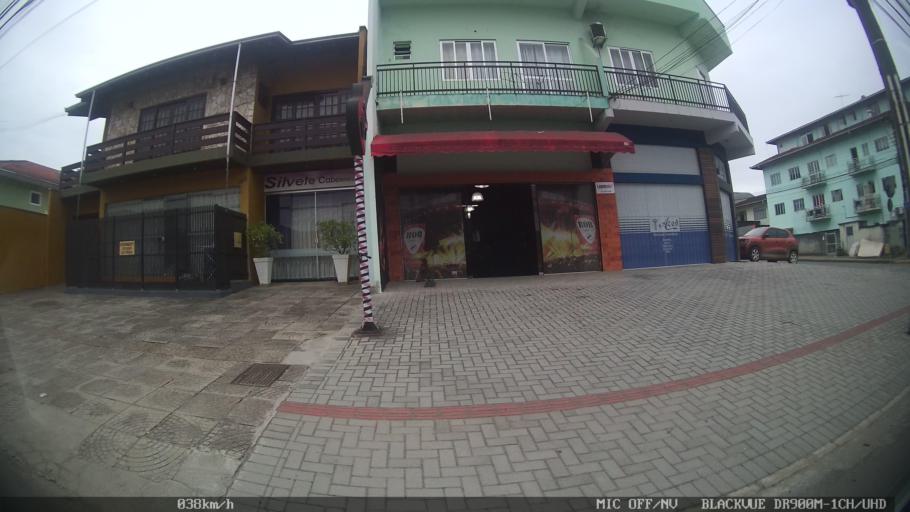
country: BR
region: Santa Catarina
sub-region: Joinville
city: Joinville
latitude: -26.2808
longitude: -48.8185
